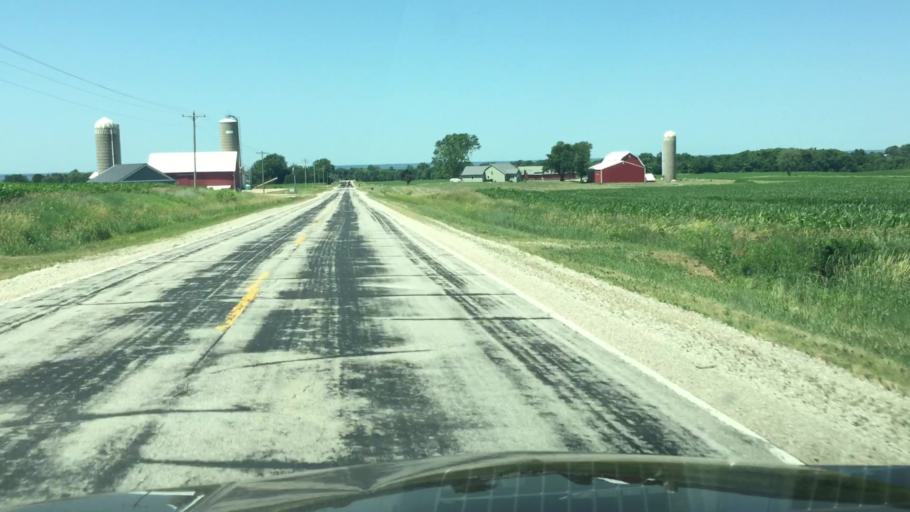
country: US
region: Wisconsin
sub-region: Calumet County
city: Chilton
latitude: 43.9697
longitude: -88.2915
